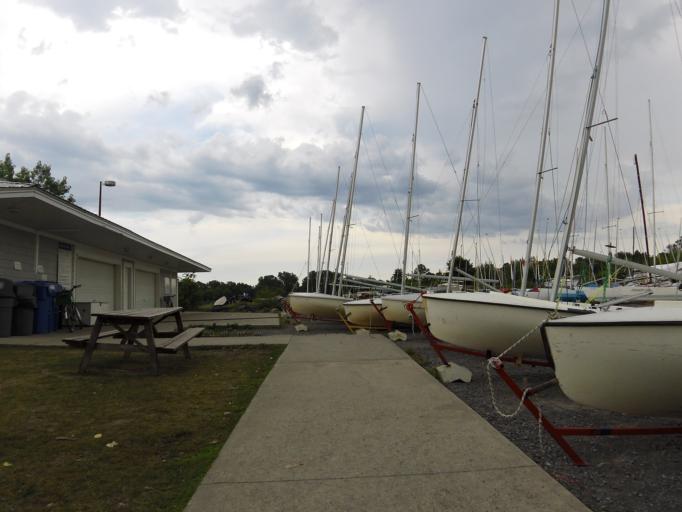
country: CA
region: Ontario
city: Bells Corners
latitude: 45.3521
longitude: -75.8249
